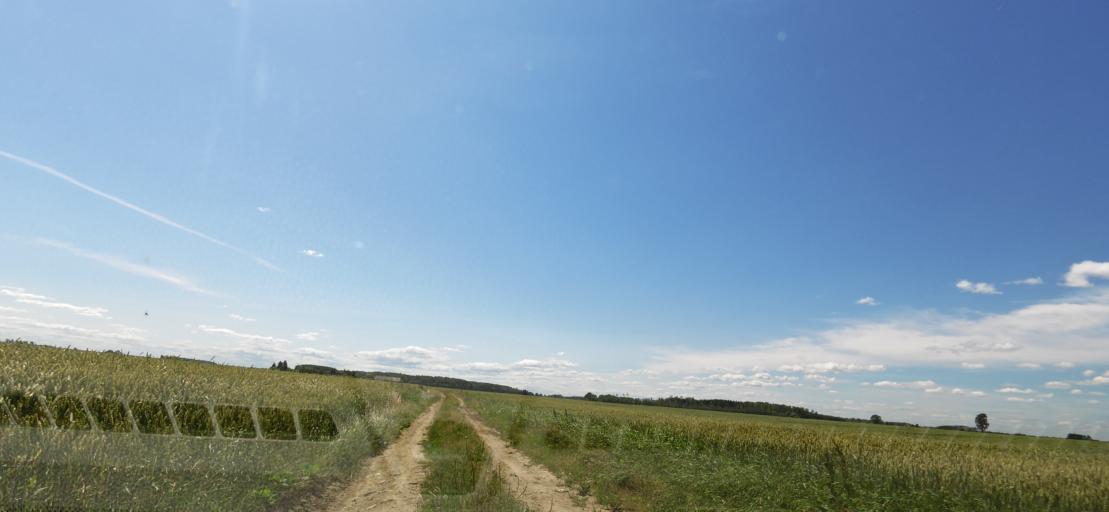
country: LT
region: Panevezys
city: Pasvalys
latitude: 56.2718
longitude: 24.5131
